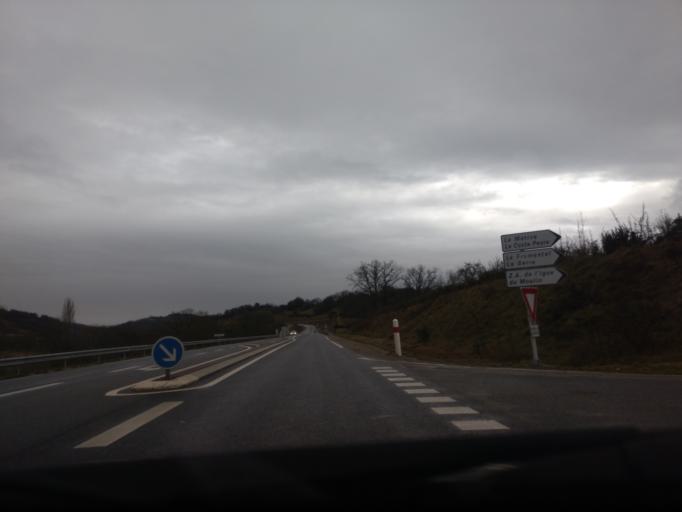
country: FR
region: Midi-Pyrenees
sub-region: Departement de l'Aveyron
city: Firmi
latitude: 44.5213
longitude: 2.3387
